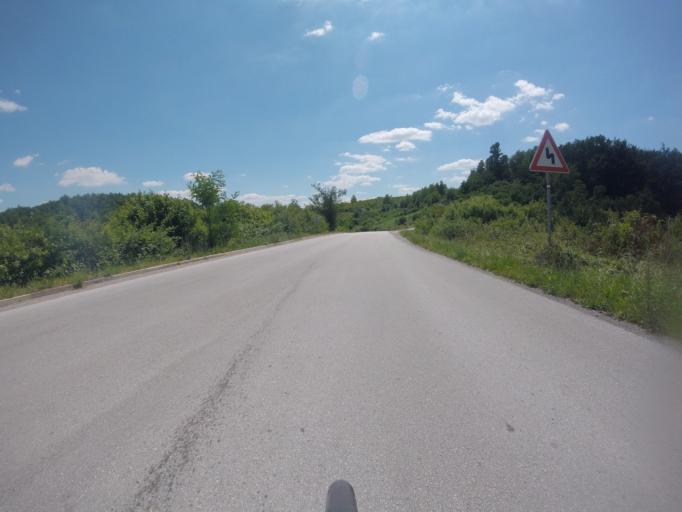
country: HR
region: Karlovacka
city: Ozalj
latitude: 45.6648
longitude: 15.4809
